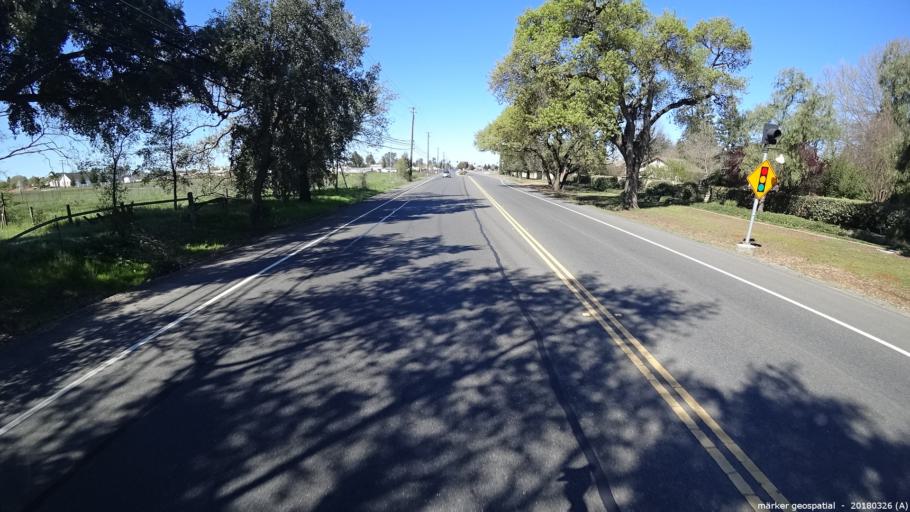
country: US
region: California
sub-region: Sacramento County
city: Vineyard
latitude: 38.4527
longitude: -121.3135
